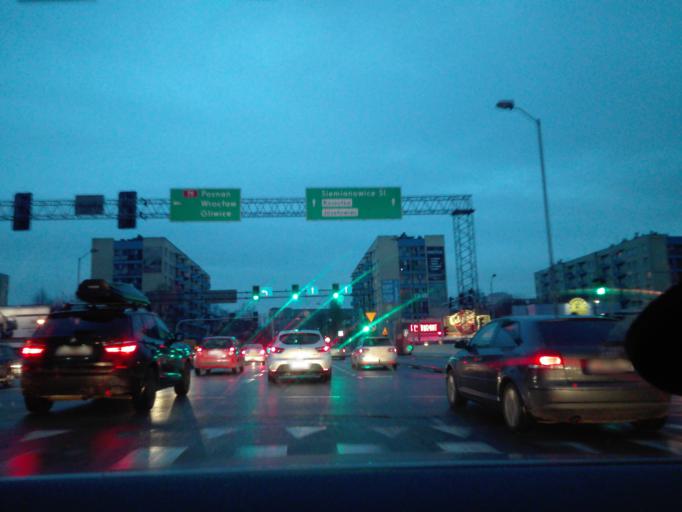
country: PL
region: Silesian Voivodeship
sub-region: Katowice
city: Katowice
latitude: 50.2650
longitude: 19.0188
